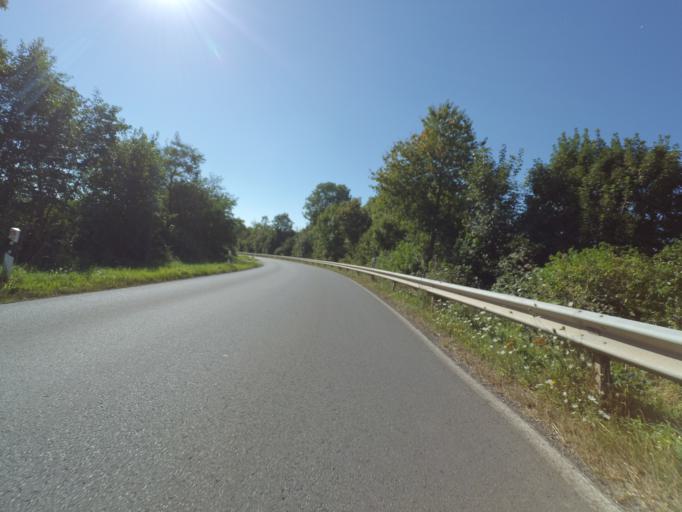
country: DE
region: Rheinland-Pfalz
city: Strohn
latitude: 50.1113
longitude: 6.9345
